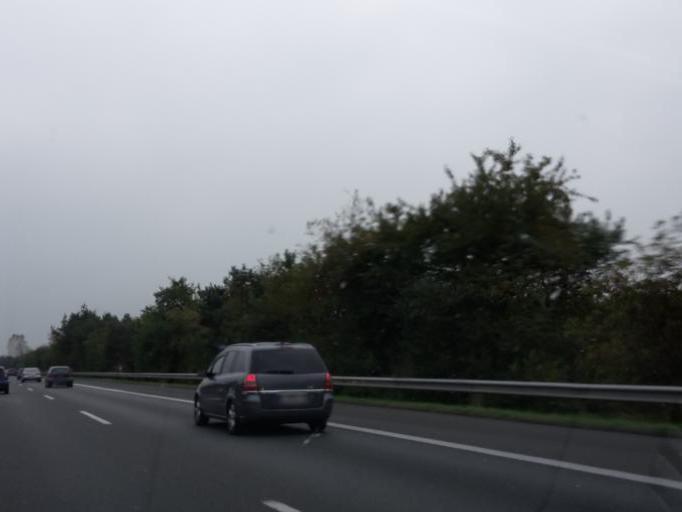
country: DE
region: Lower Saxony
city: Holdorf
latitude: 52.5704
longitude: 8.1104
